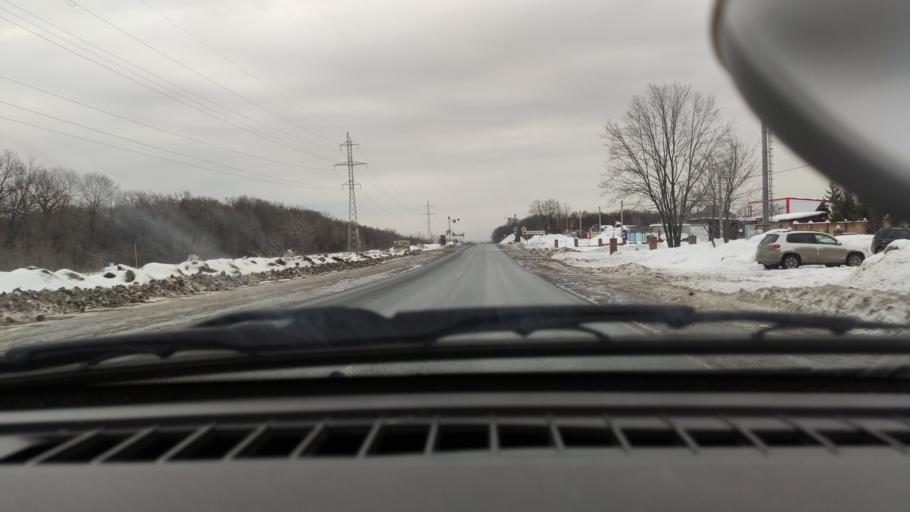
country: RU
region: Samara
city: Novosemeykino
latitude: 53.3337
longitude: 50.2544
